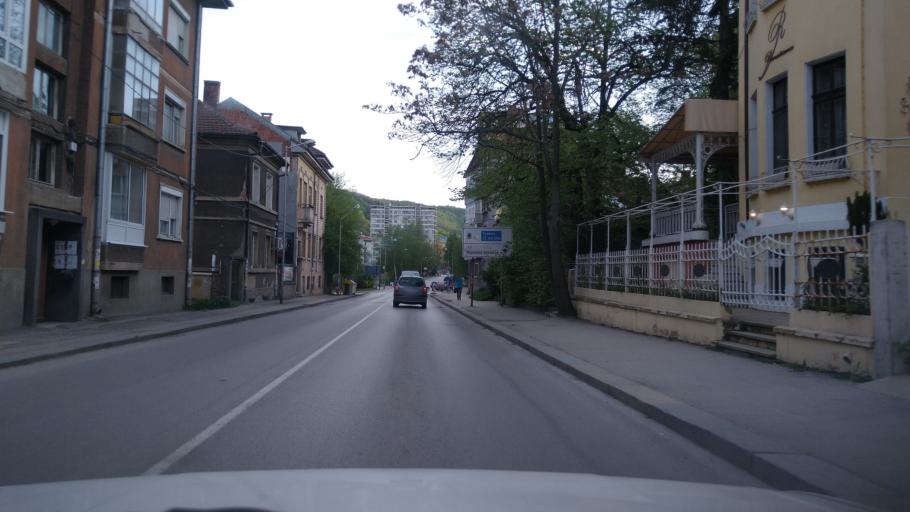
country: BG
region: Gabrovo
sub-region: Obshtina Gabrovo
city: Gabrovo
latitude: 42.8740
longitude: 25.3162
